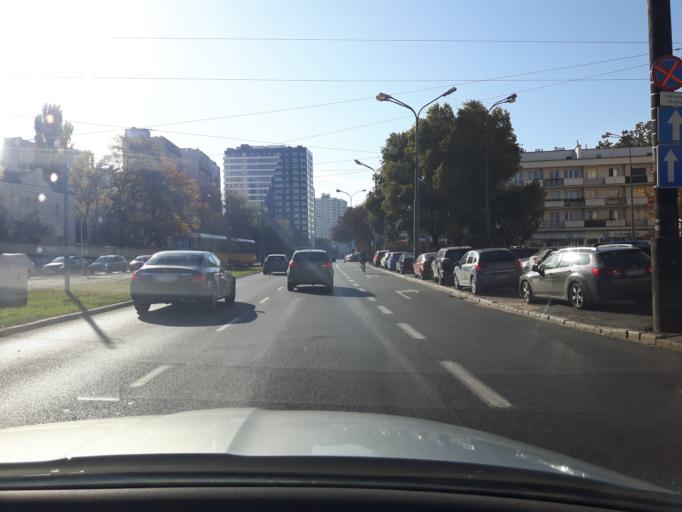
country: PL
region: Masovian Voivodeship
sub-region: Warszawa
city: Wola
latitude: 52.2350
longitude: 20.9725
